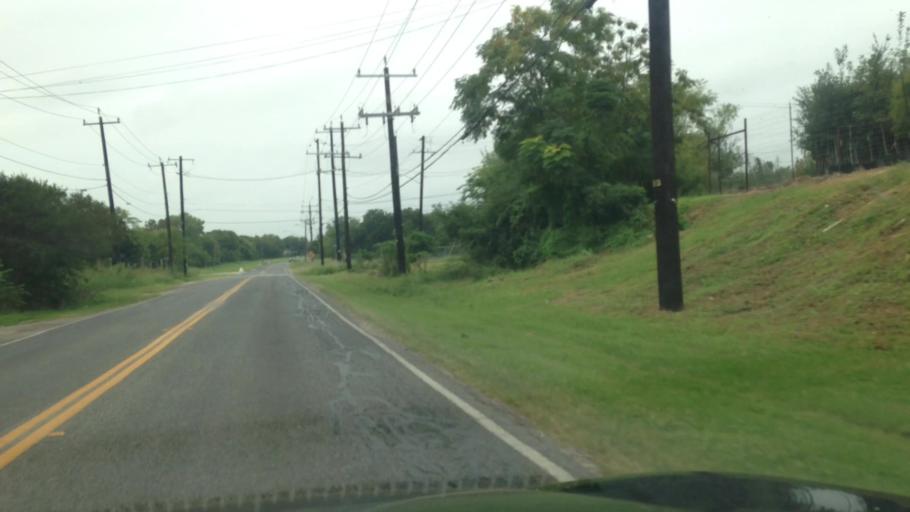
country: US
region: Texas
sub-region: Bexar County
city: Windcrest
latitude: 29.5751
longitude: -98.4045
